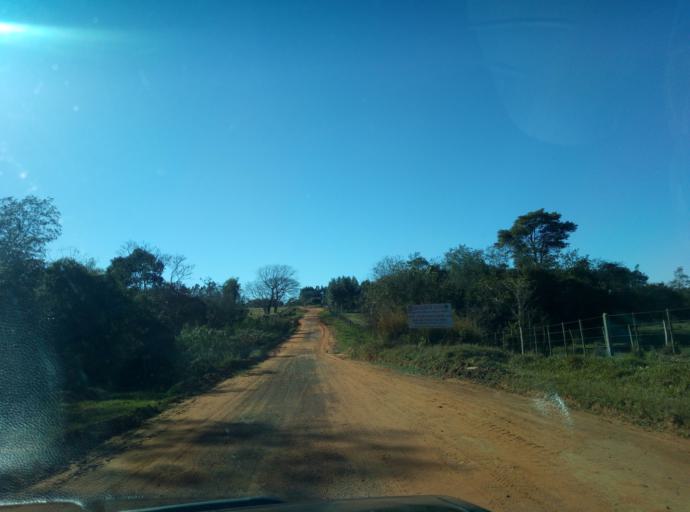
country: PY
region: Caaguazu
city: Doctor Cecilio Baez
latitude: -25.1640
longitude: -56.2551
